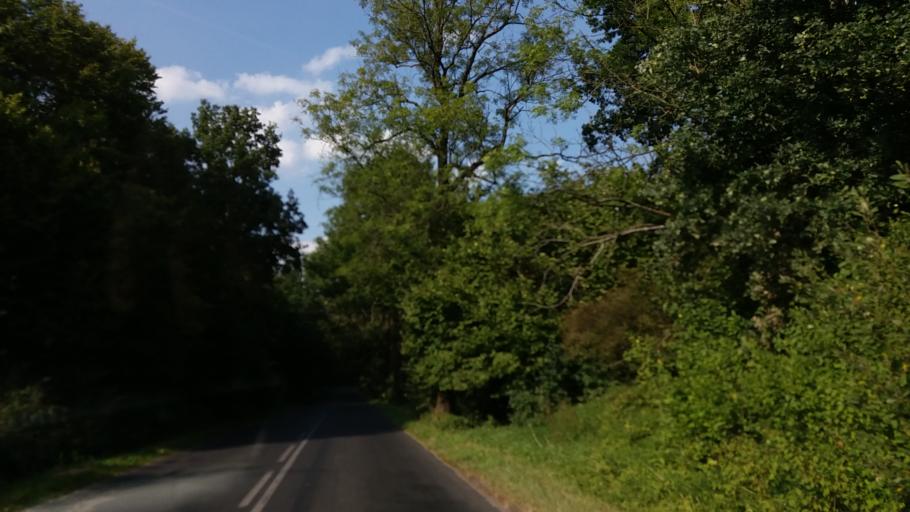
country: PL
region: West Pomeranian Voivodeship
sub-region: Powiat choszczenski
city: Choszczno
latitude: 53.1419
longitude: 15.4516
